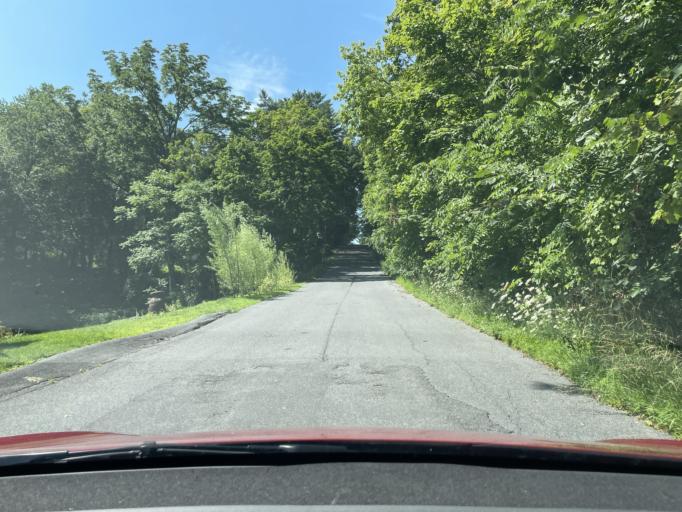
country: US
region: New York
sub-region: Ulster County
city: Saugerties South
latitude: 42.0689
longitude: -73.9457
